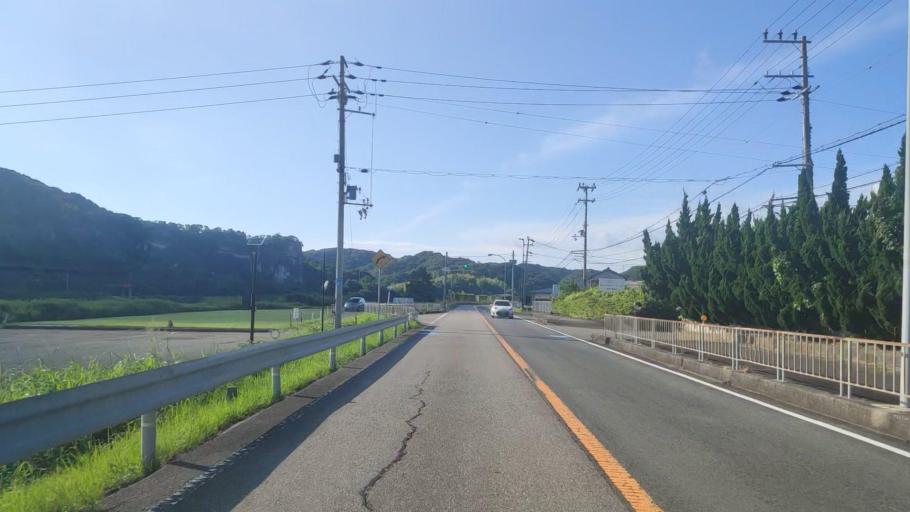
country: JP
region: Wakayama
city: Tanabe
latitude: 33.6606
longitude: 135.3993
